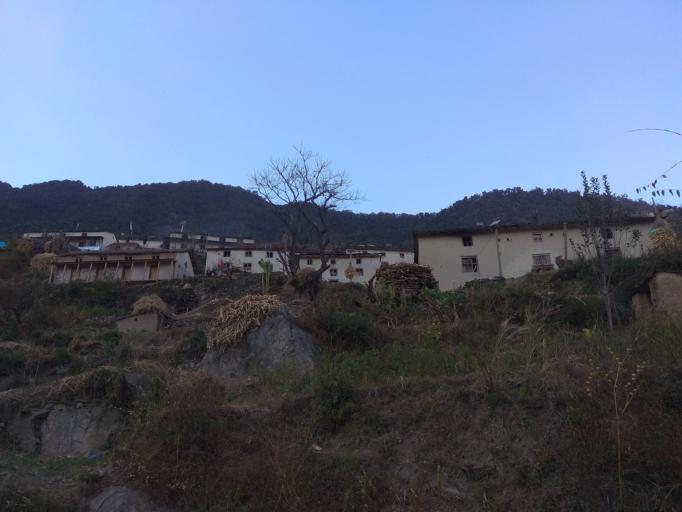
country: NP
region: Mid Western
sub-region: Karnali Zone
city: Jumla
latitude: 29.3253
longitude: 81.7234
